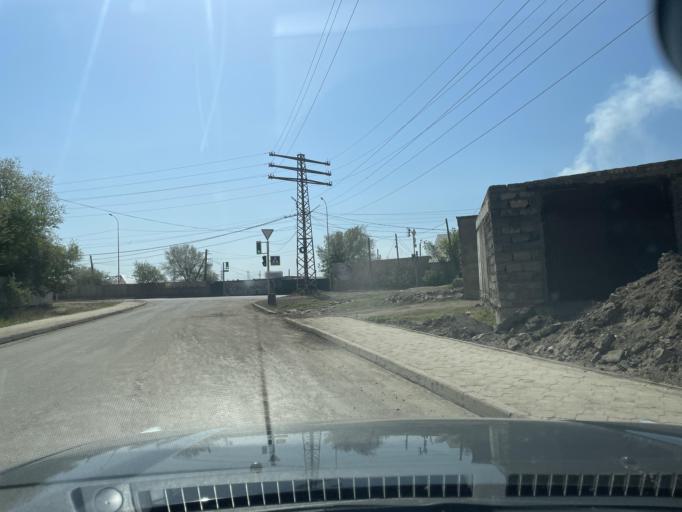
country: KZ
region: Qaraghandy
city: Zhezqazghan
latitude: 47.7880
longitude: 67.7137
